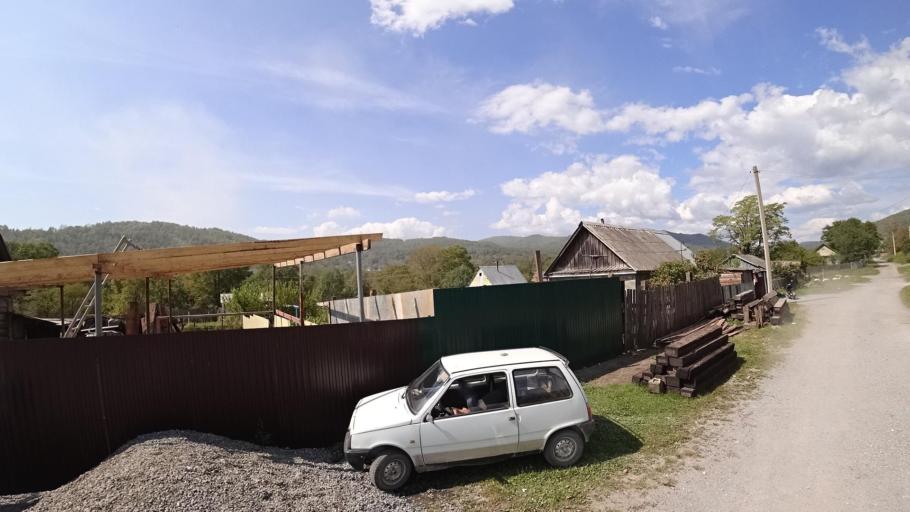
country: RU
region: Jewish Autonomous Oblast
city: Londoko
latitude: 49.0222
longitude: 131.9336
